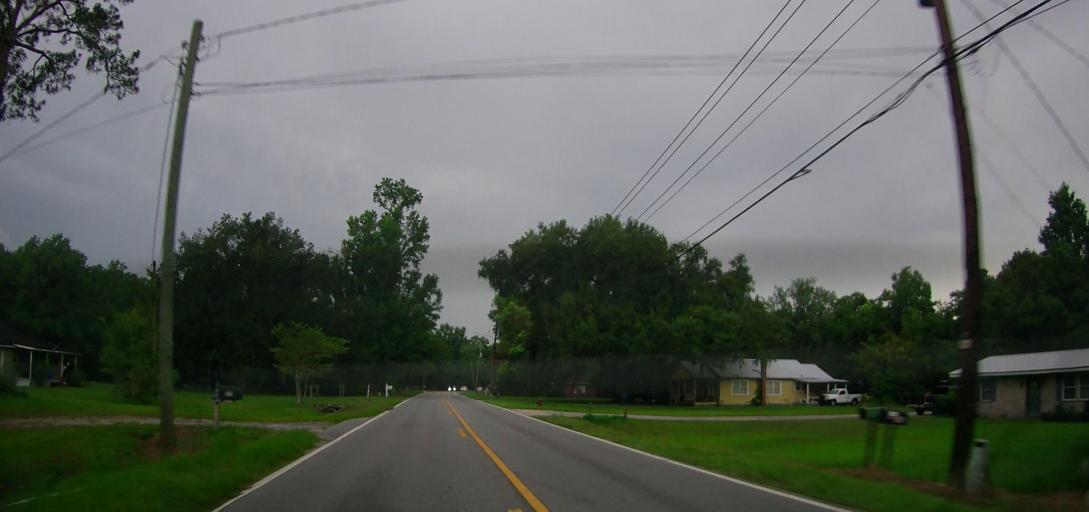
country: US
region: Georgia
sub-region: Glynn County
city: Dock Junction
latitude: 31.2261
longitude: -81.5119
